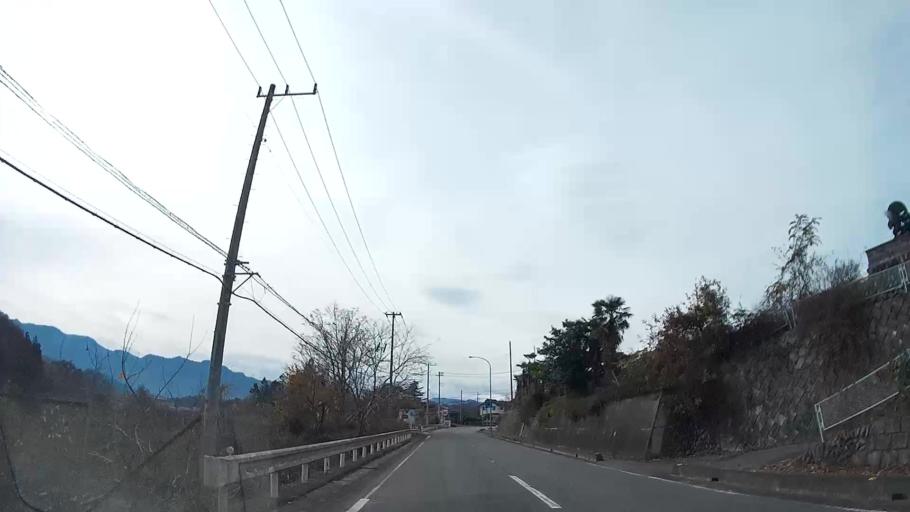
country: JP
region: Saitama
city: Chichibu
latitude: 35.9998
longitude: 139.0347
